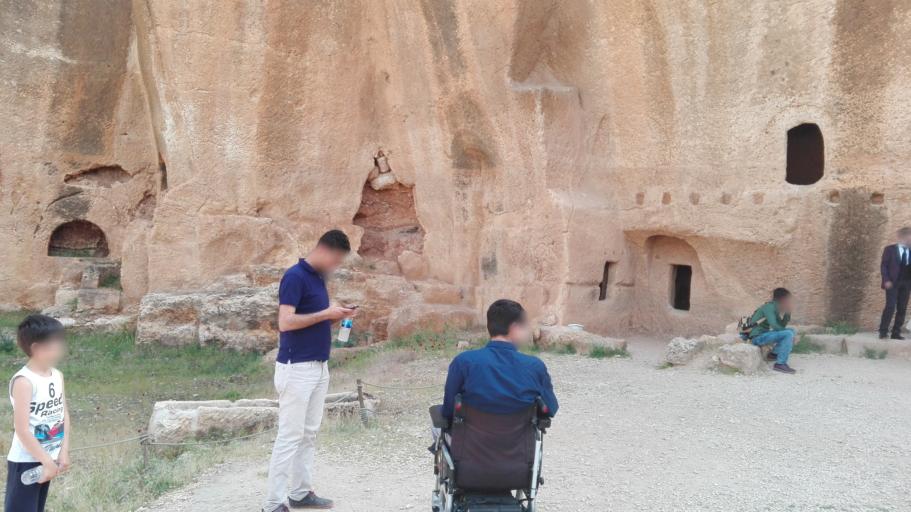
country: TR
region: Mardin
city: Oguz
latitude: 37.1779
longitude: 40.9476
